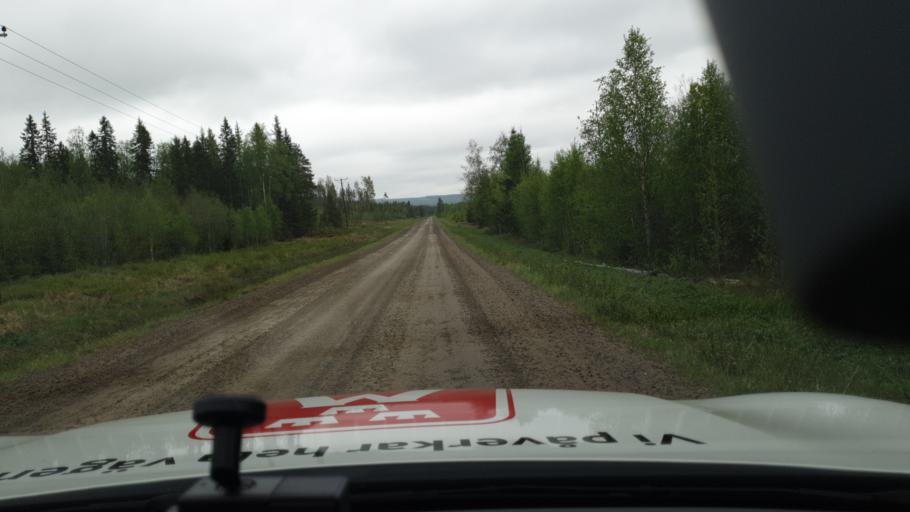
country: SE
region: Vaesterbotten
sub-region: Vannas Kommun
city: Vannasby
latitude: 64.0113
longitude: 19.8774
